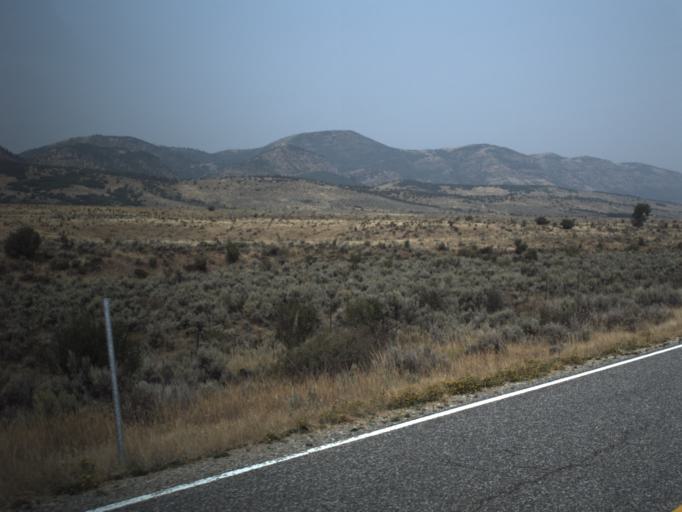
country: US
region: Utah
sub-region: Morgan County
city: Morgan
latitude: 40.9616
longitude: -111.5471
